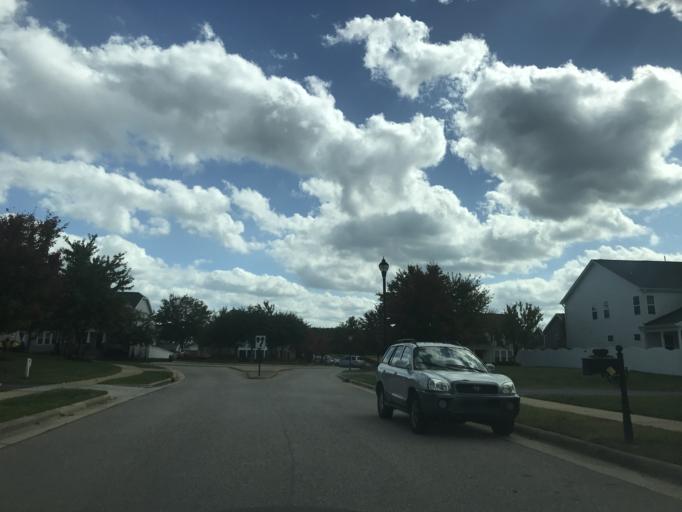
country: US
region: North Carolina
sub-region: Wake County
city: Raleigh
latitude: 35.7362
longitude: -78.6590
